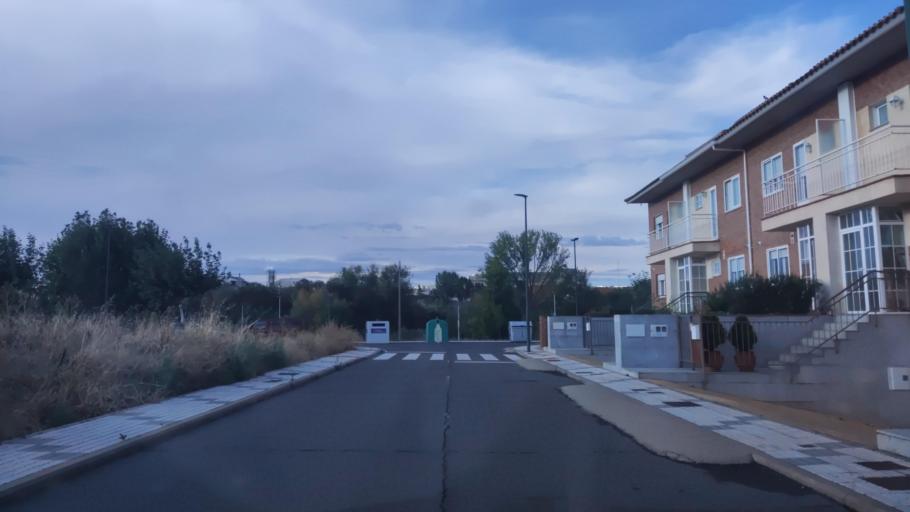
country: ES
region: Castille and Leon
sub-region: Provincia de Salamanca
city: Salamanca
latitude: 40.9543
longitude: -5.6518
